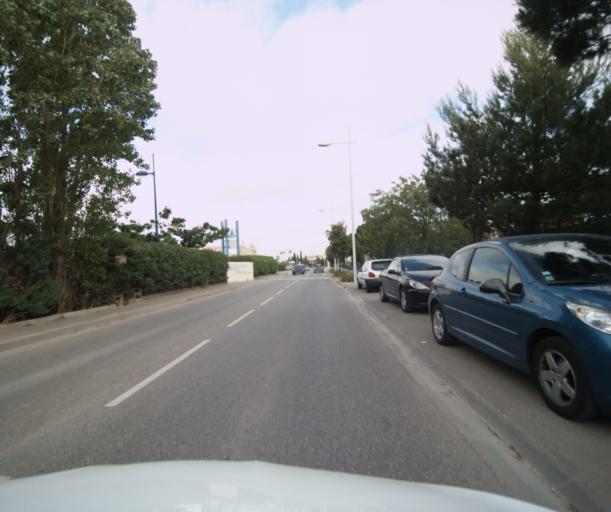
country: FR
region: Provence-Alpes-Cote d'Azur
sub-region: Departement du Var
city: Six-Fours-les-Plages
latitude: 43.1168
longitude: 5.8466
